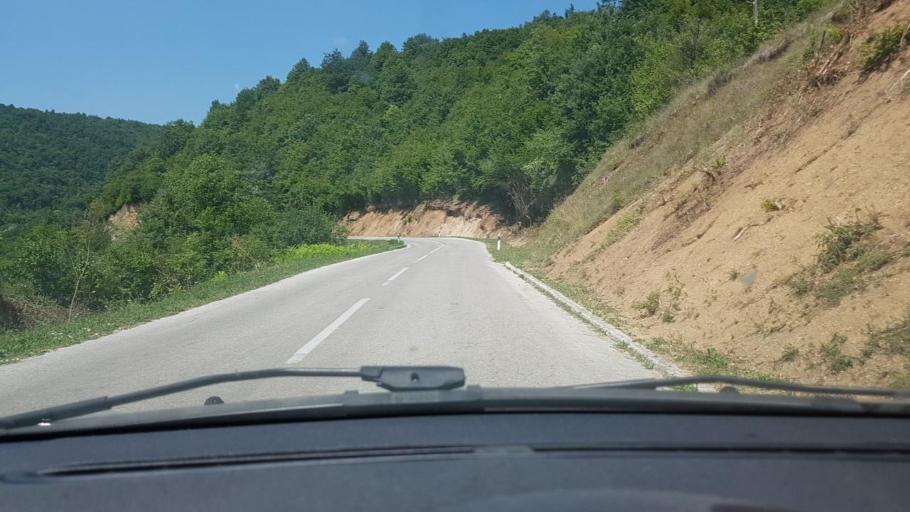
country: BA
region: Federation of Bosnia and Herzegovina
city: Orasac
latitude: 44.5730
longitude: 16.0821
